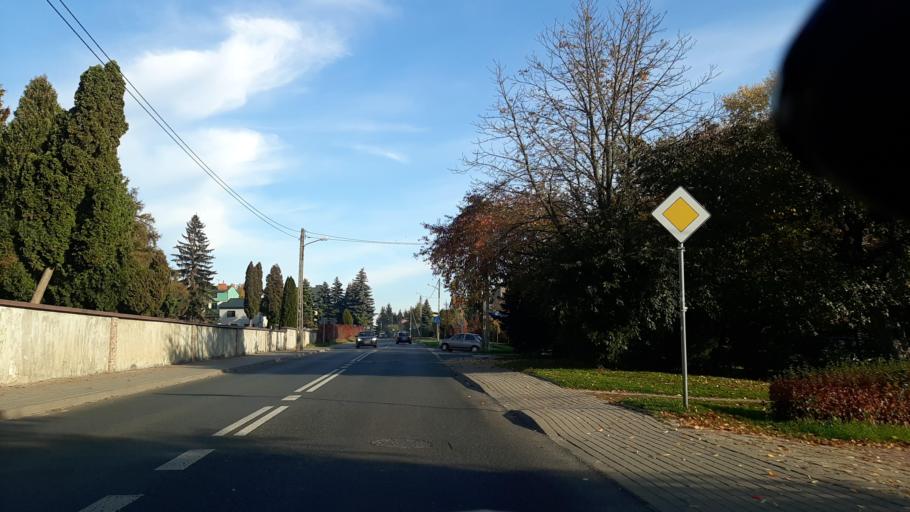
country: PL
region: Lublin Voivodeship
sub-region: Powiat lubelski
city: Lublin
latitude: 51.2642
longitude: 22.5812
